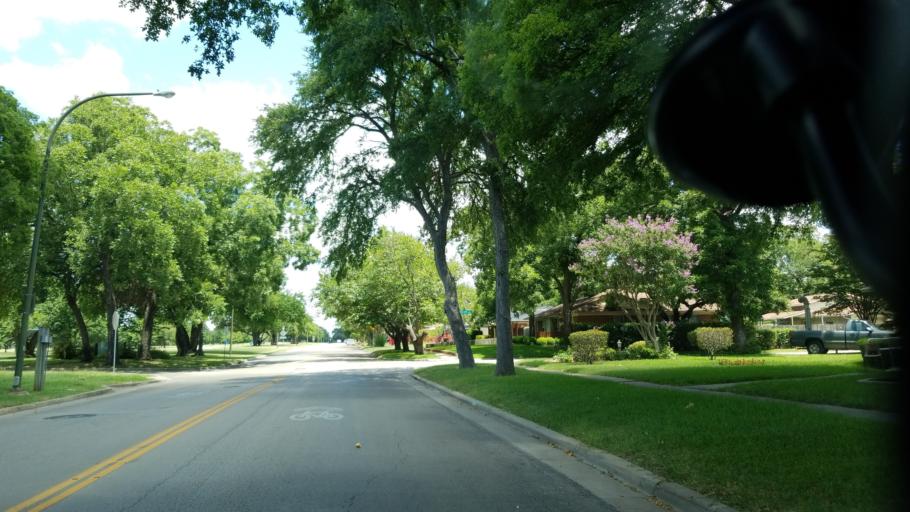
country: US
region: Texas
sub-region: Dallas County
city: Cockrell Hill
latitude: 32.7087
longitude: -96.8486
